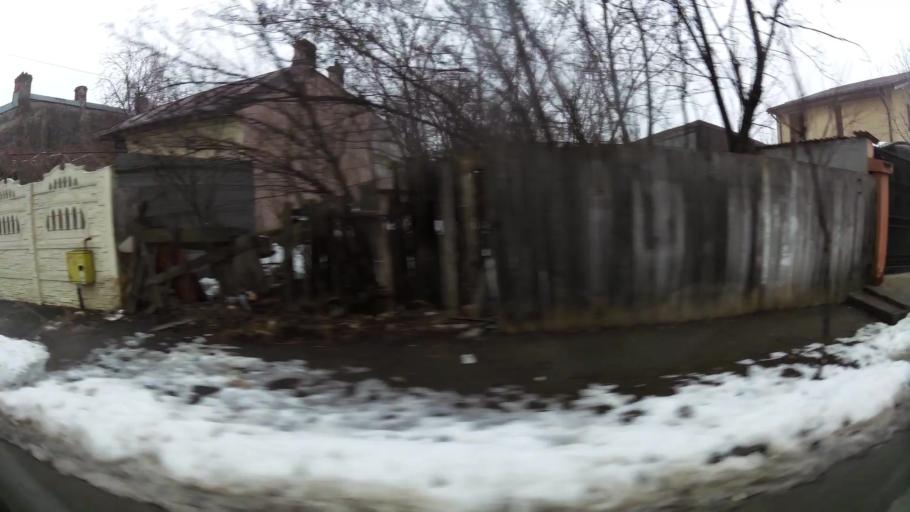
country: RO
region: Ilfov
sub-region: Comuna Chiajna
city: Chiajna
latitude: 44.4600
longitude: 25.9778
